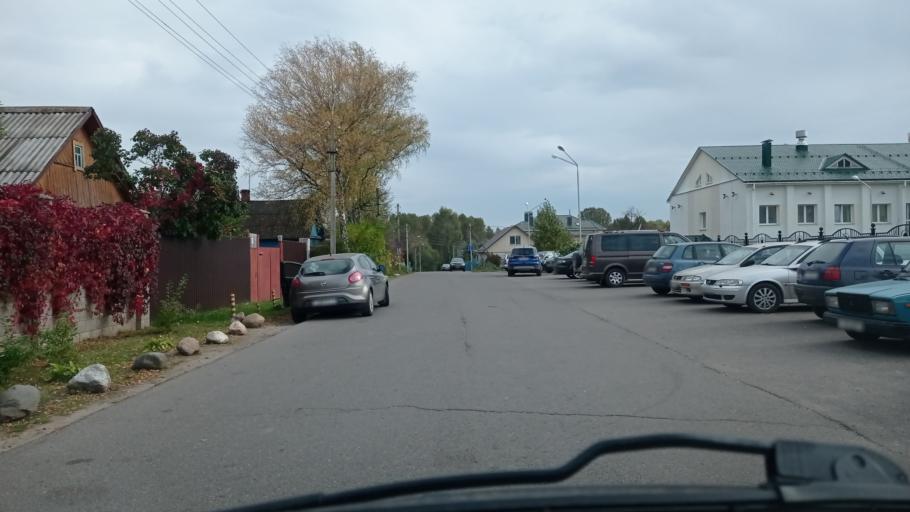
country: BY
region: Vitebsk
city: Vitebsk
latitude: 55.1853
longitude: 30.2123
